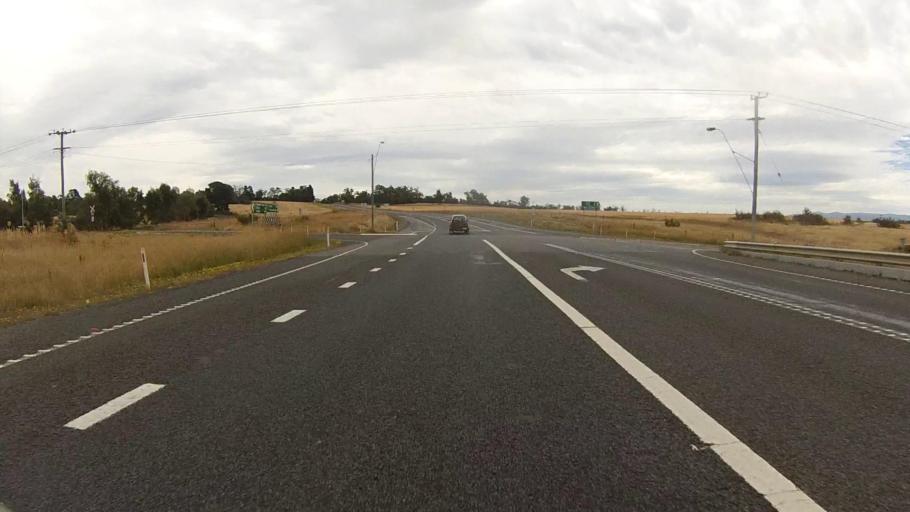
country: AU
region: Tasmania
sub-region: Northern Midlands
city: Evandale
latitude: -41.8368
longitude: 147.4478
